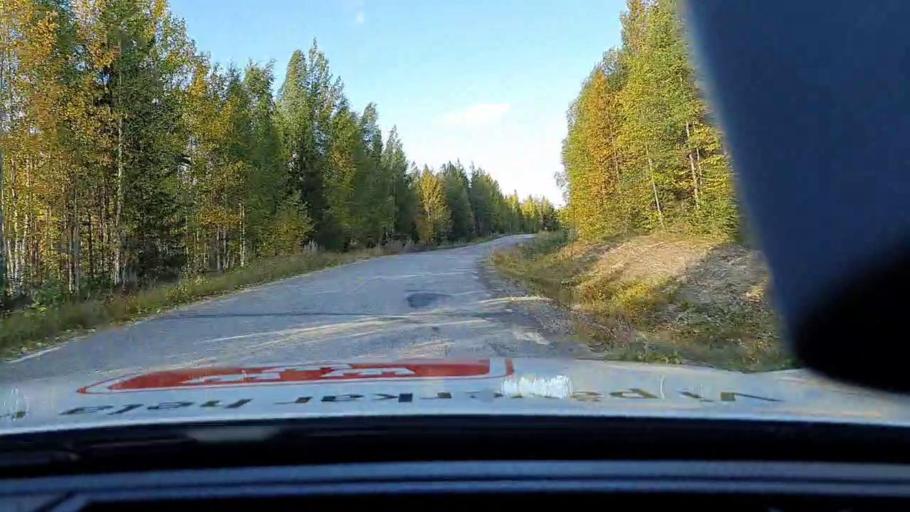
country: SE
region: Norrbotten
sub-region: Pitea Kommun
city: Norrfjarden
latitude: 65.6478
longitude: 21.4547
